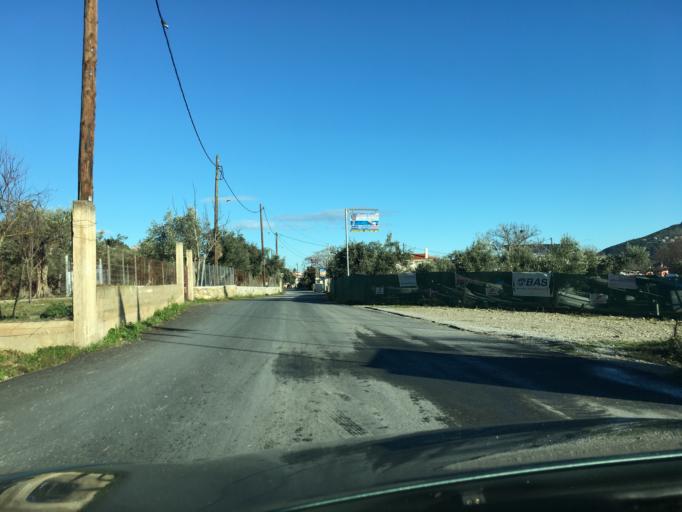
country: GR
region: Thessaly
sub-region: Nomos Magnisias
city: Skopelos
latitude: 39.1119
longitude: 23.7252
